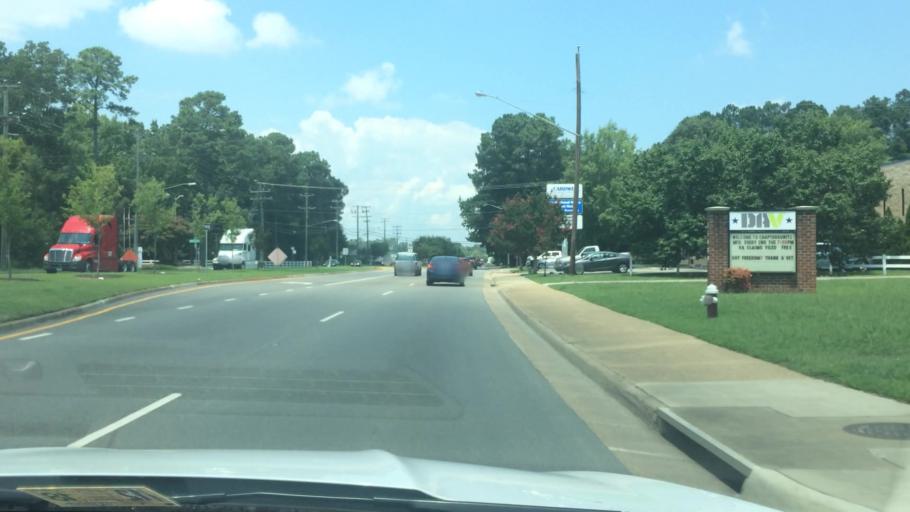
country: US
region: Virginia
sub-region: York County
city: Yorktown
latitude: 37.1532
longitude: -76.5546
